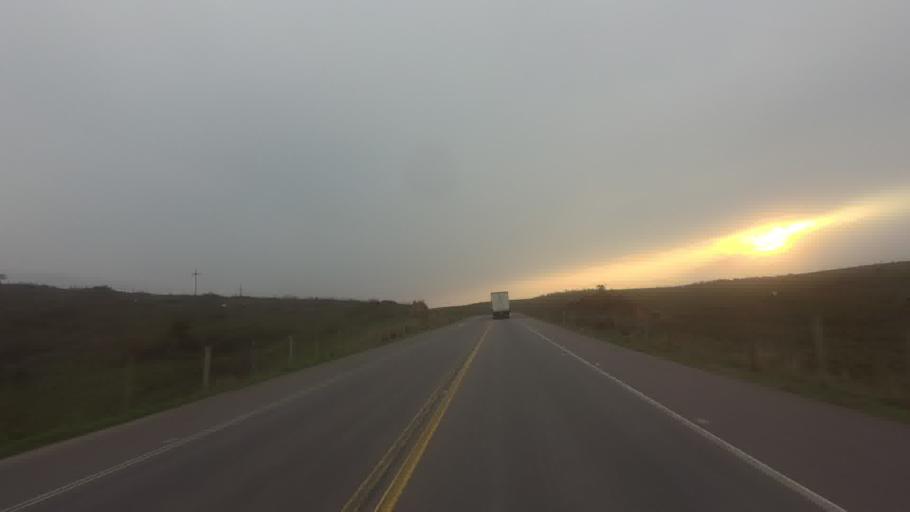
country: BR
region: Minas Gerais
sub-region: Recreio
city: Recreio
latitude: -21.6797
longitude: -42.3964
